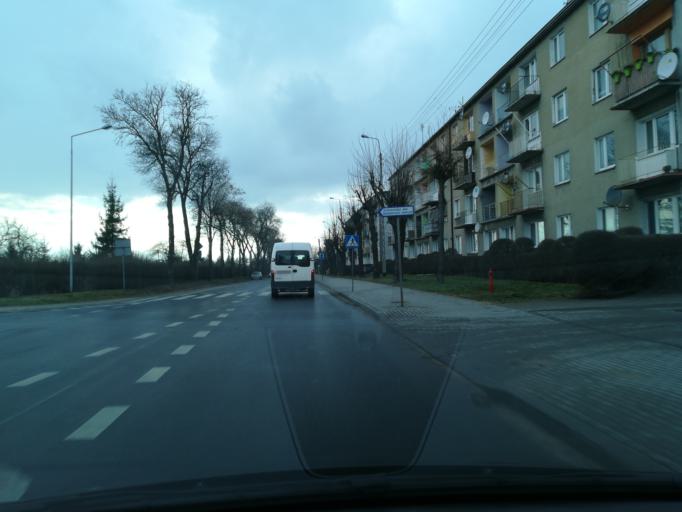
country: PL
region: Lodz Voivodeship
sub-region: Powiat radomszczanski
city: Radomsko
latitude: 51.0714
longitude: 19.4249
